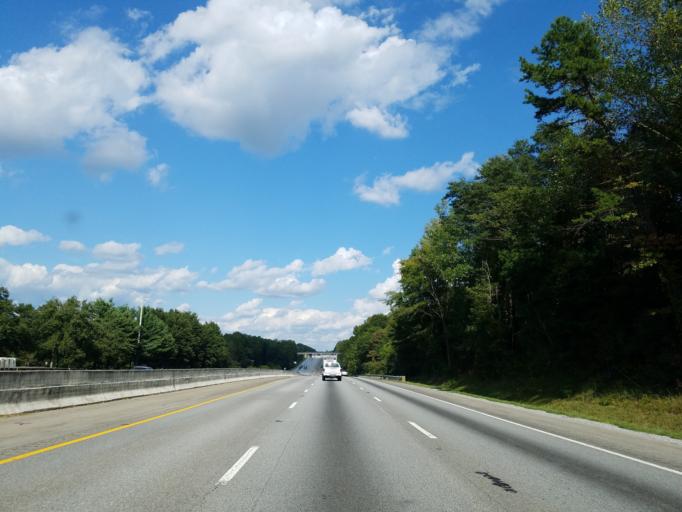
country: US
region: South Carolina
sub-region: Anderson County
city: Northlake
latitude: 34.5999
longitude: -82.6540
